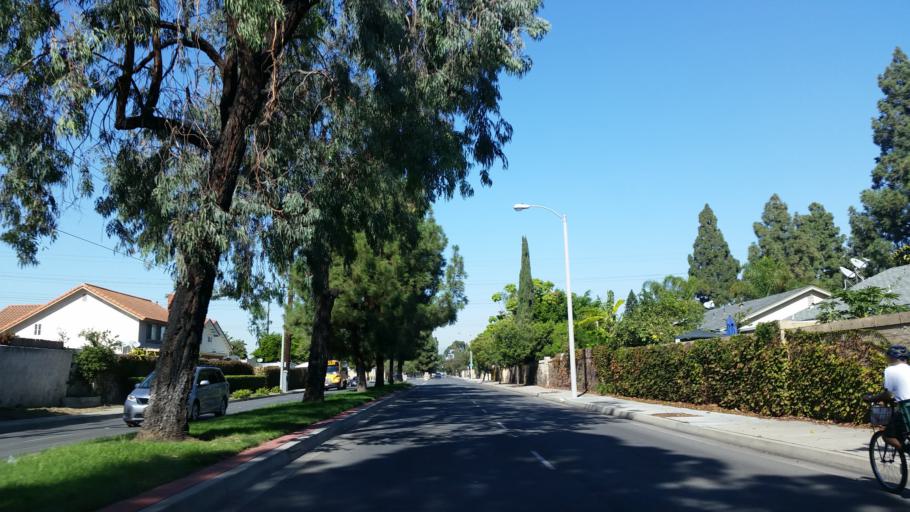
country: US
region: California
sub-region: Los Angeles County
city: Cerritos
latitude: 33.8480
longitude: -118.0721
